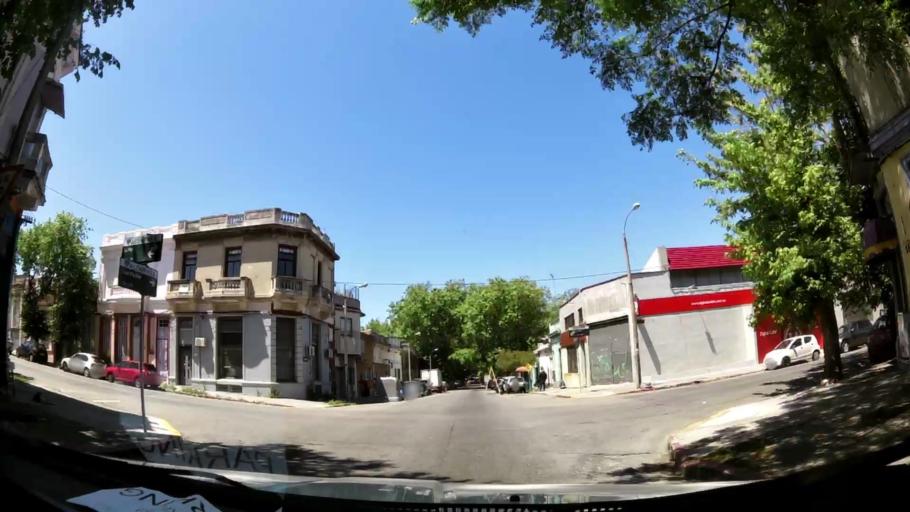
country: UY
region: Montevideo
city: Montevideo
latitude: -34.8940
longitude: -56.1701
